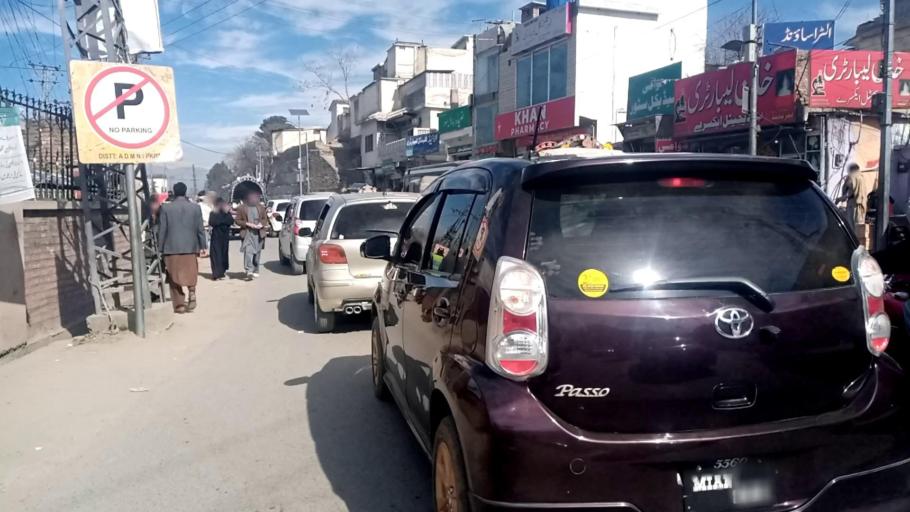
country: PK
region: Khyber Pakhtunkhwa
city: Saidu Sharif
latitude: 34.7498
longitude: 72.3573
